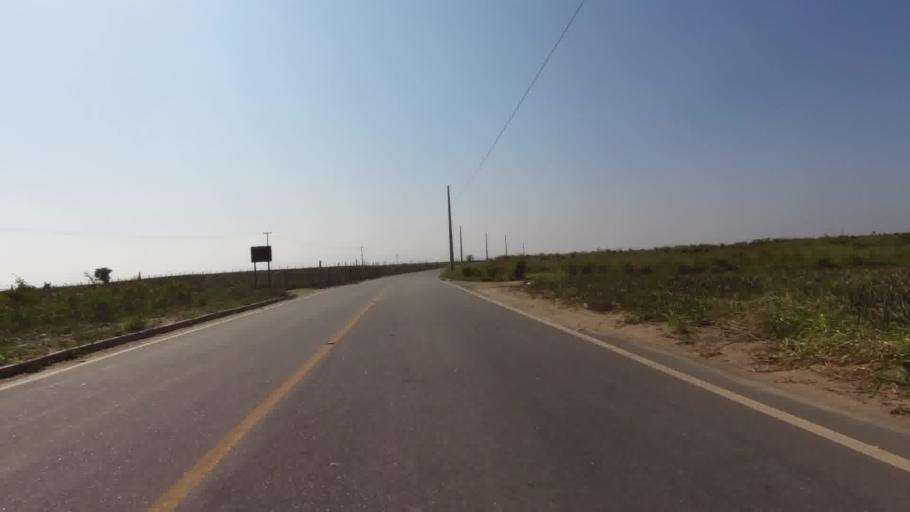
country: BR
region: Espirito Santo
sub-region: Itapemirim
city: Itapemirim
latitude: -21.0272
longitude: -40.8382
